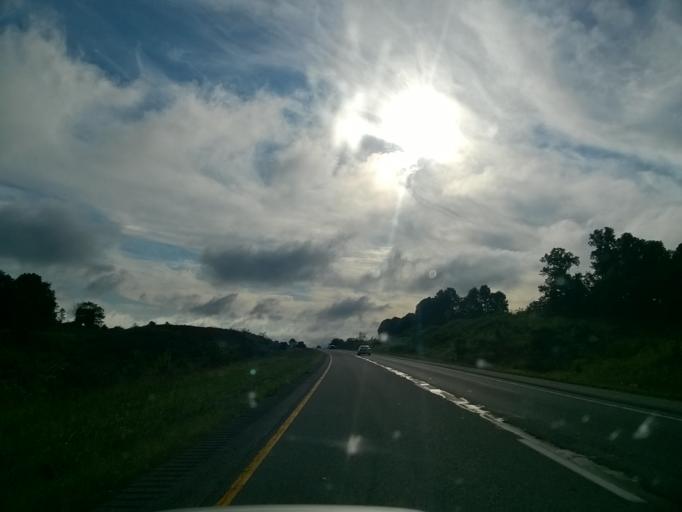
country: US
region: Indiana
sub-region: Dubois County
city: Ferdinand
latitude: 38.2021
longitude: -86.8299
